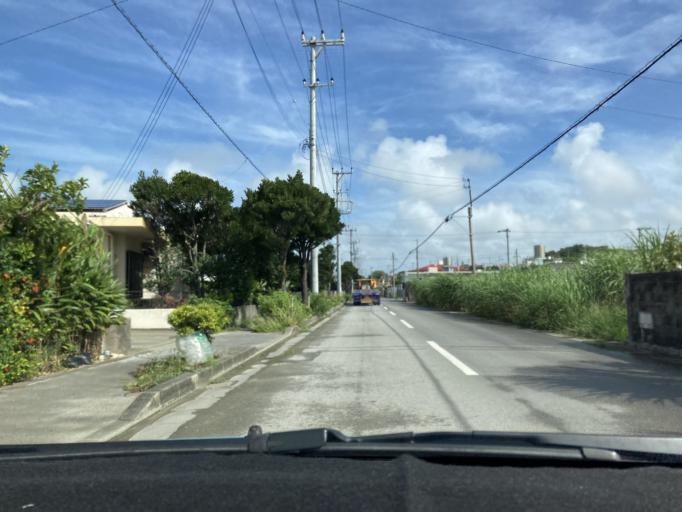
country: JP
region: Okinawa
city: Itoman
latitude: 26.1020
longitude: 127.6618
